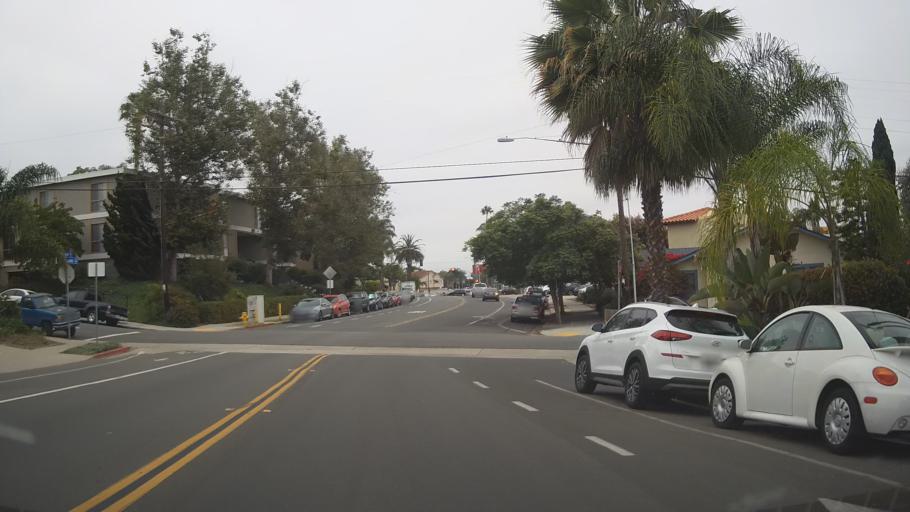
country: US
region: California
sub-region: San Diego County
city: San Diego
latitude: 32.7538
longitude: -117.1499
